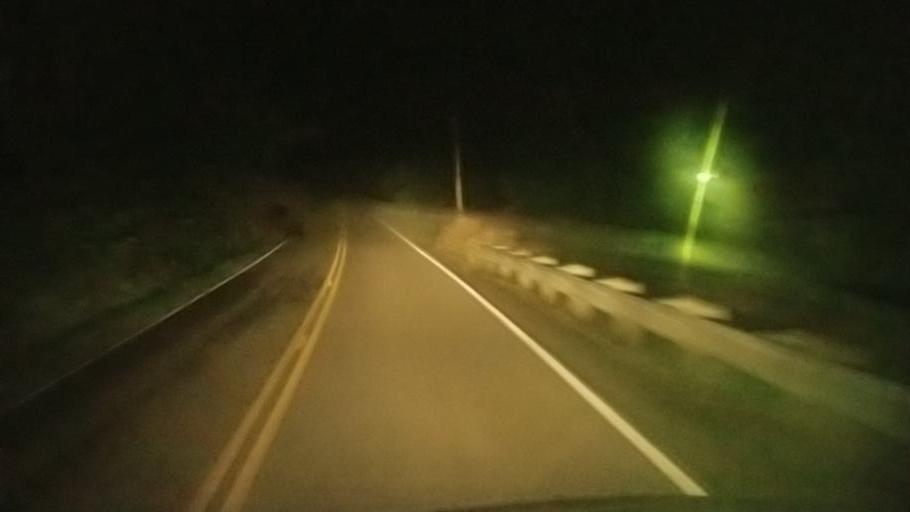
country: US
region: Ohio
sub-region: Knox County
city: Oak Hill
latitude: 40.4125
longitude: -82.0937
